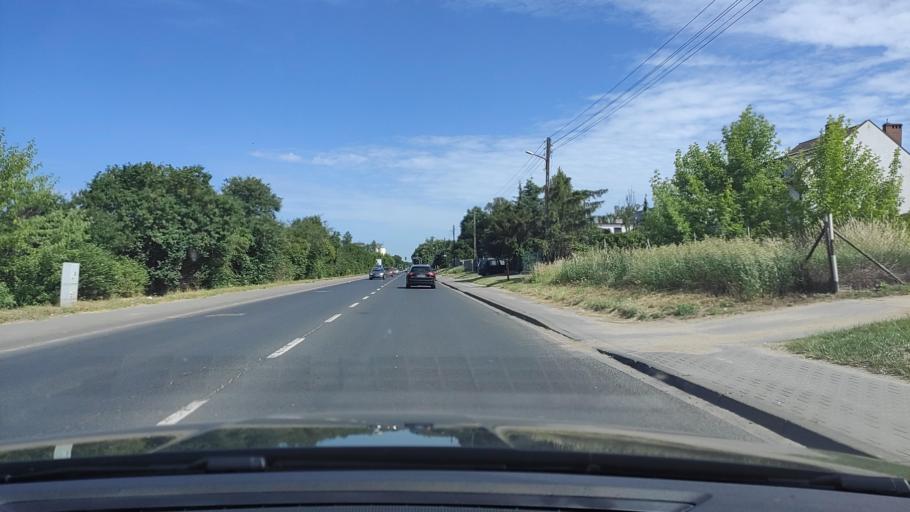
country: PL
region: Greater Poland Voivodeship
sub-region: Powiat poznanski
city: Czerwonak
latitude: 52.4774
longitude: 16.9791
